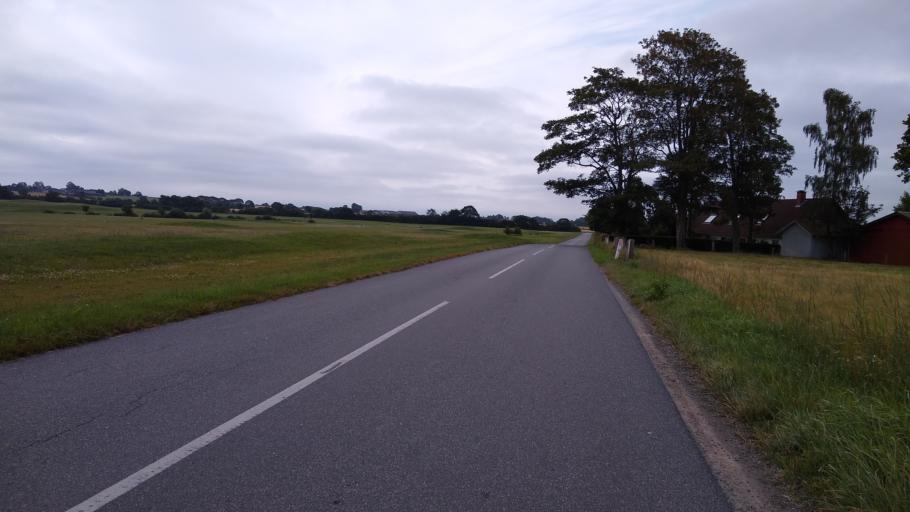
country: DK
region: South Denmark
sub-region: Vejle Kommune
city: Brejning
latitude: 55.6521
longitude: 9.6831
